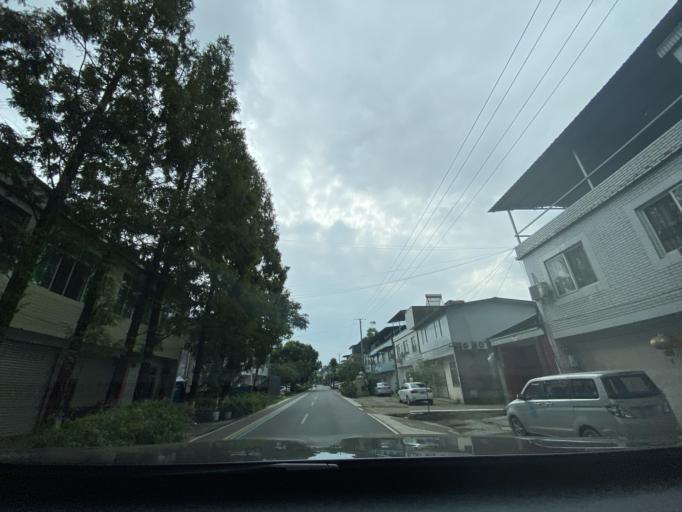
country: CN
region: Sichuan
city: Wujin
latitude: 30.4046
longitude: 103.9874
